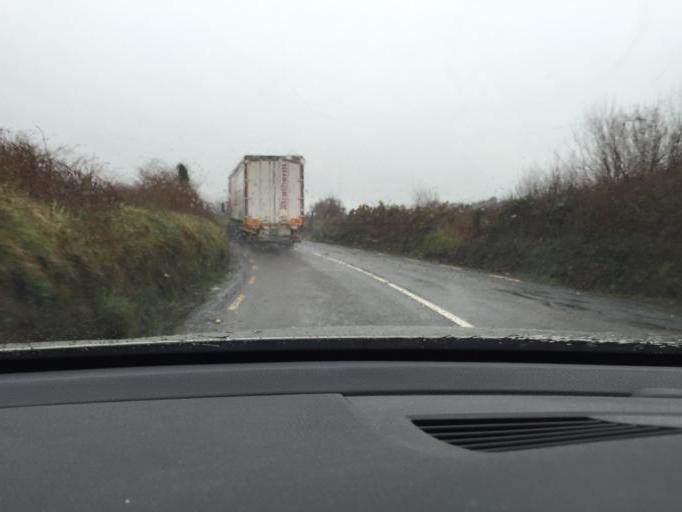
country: IE
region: Munster
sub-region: Ciarrai
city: Dingle
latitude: 52.1459
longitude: -10.1267
